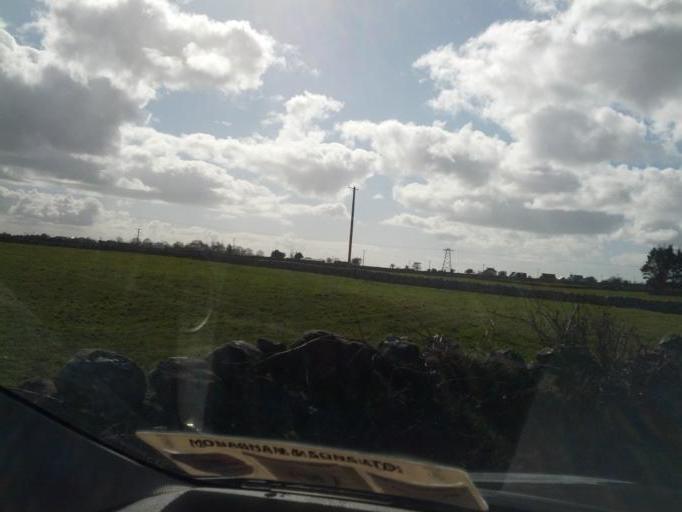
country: IE
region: Connaught
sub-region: County Galway
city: Oranmore
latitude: 53.3130
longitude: -8.8868
